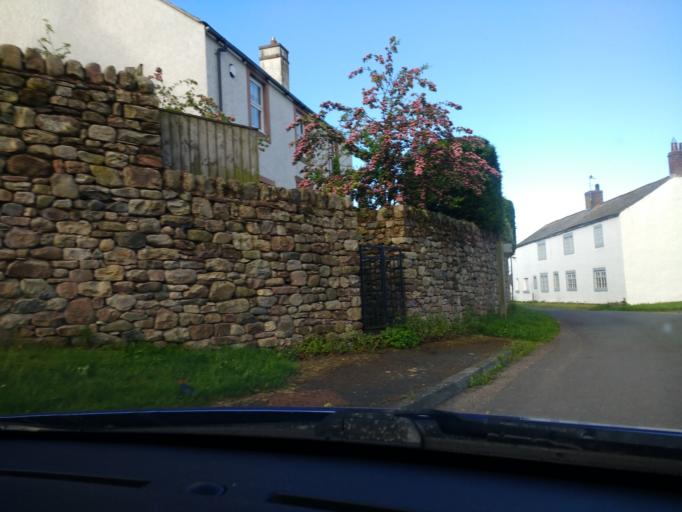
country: GB
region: England
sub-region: Cumbria
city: Appleby-in-Westmorland
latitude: 54.6757
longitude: -2.5650
